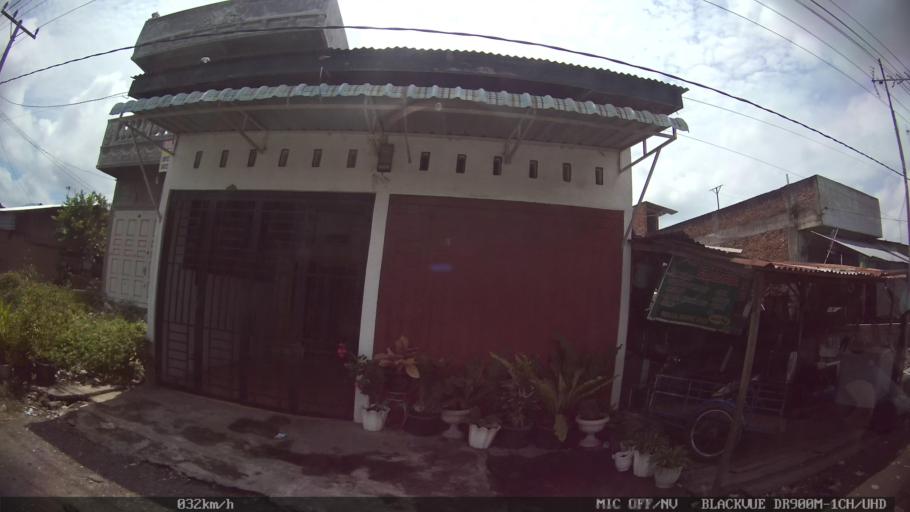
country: ID
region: North Sumatra
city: Percut
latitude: 3.6159
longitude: 98.7632
